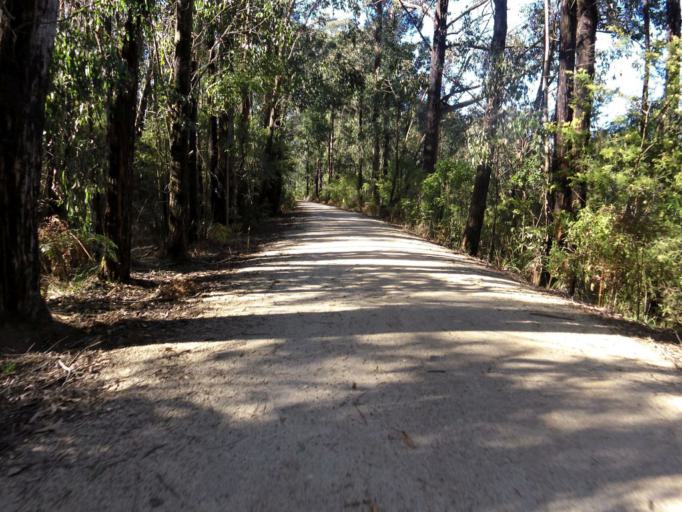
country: AU
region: Victoria
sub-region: Latrobe
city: Moe
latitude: -38.3874
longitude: 146.1886
